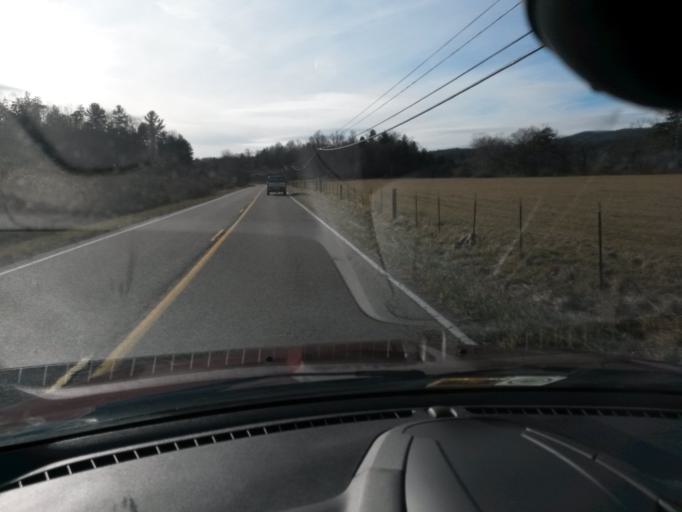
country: US
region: Virginia
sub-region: Rockbridge County
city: East Lexington
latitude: 38.0733
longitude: -79.3953
